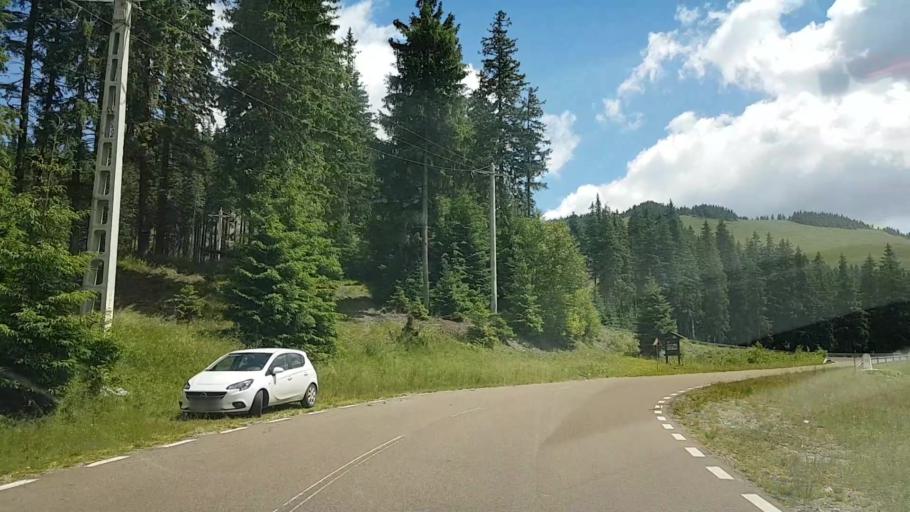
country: RO
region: Suceava
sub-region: Comuna Sadova
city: Sadova
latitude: 47.4581
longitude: 25.5220
